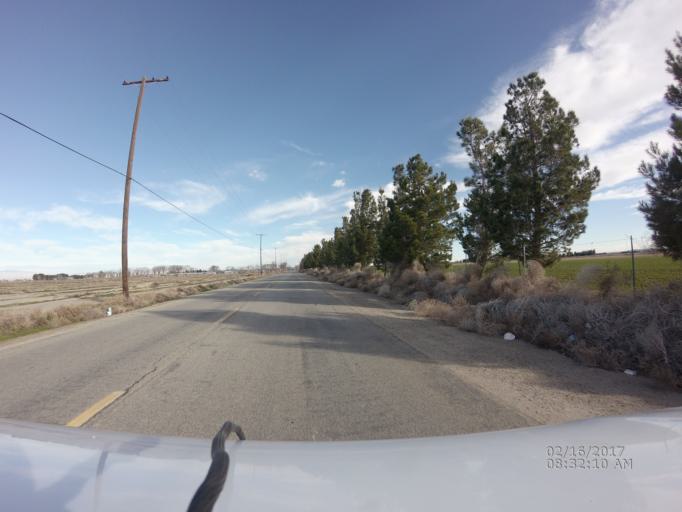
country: US
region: California
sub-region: Los Angeles County
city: Lancaster
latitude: 34.7133
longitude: -118.0054
